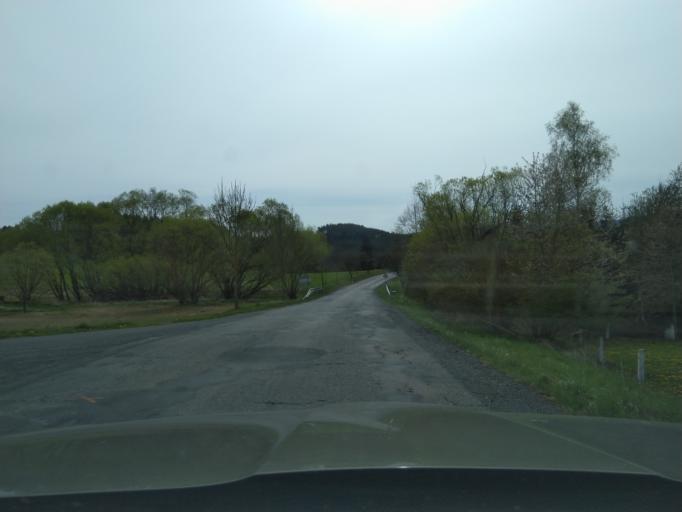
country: CZ
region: Plzensky
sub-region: Okres Klatovy
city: Kasperske Hory
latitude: 49.1957
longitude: 13.6191
